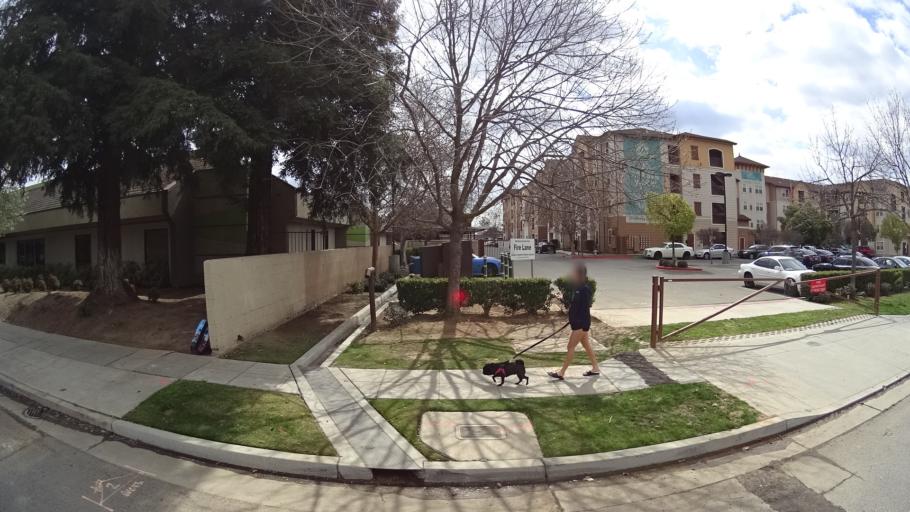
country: US
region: California
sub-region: Fresno County
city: Fresno
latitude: 36.8157
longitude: -119.7829
